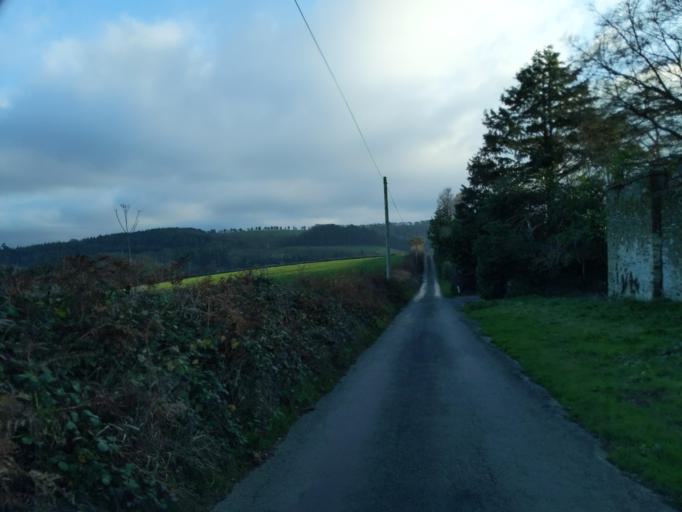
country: GB
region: England
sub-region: Cornwall
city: Pillaton
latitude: 50.3941
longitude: -4.3274
